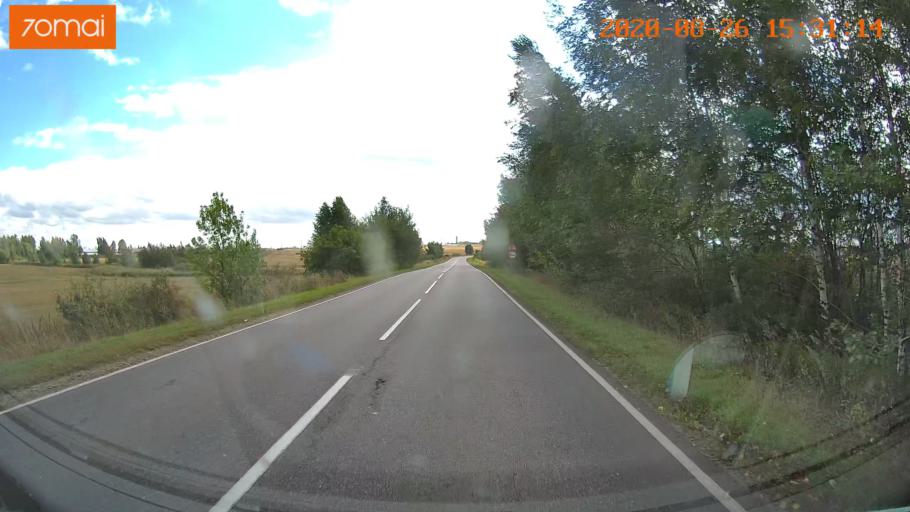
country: RU
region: Tula
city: Severo-Zadonsk
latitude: 54.0820
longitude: 38.3892
